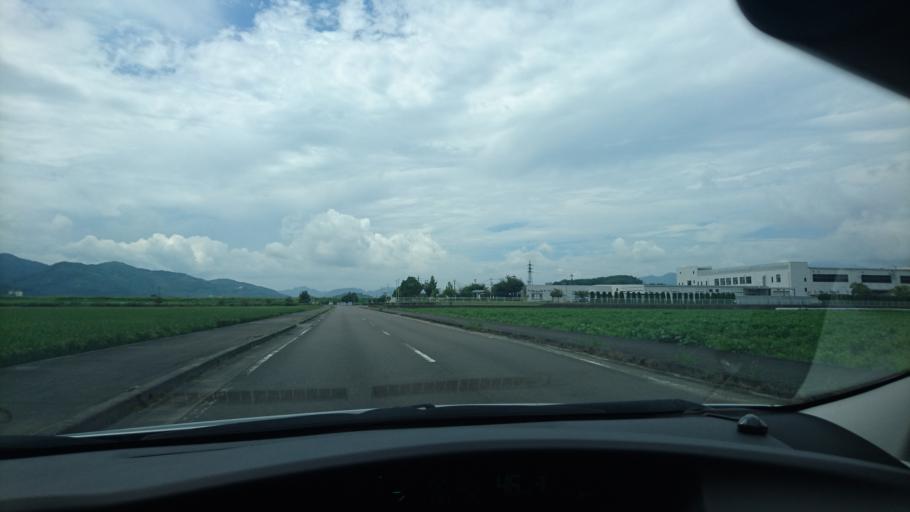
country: JP
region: Saga Prefecture
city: Takeocho-takeo
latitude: 33.2103
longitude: 130.1148
